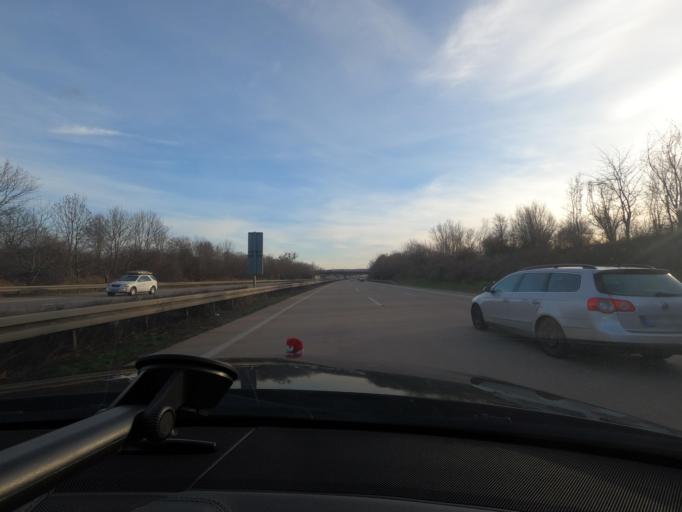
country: DE
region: Lower Saxony
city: Harsum
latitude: 52.1771
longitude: 9.9780
